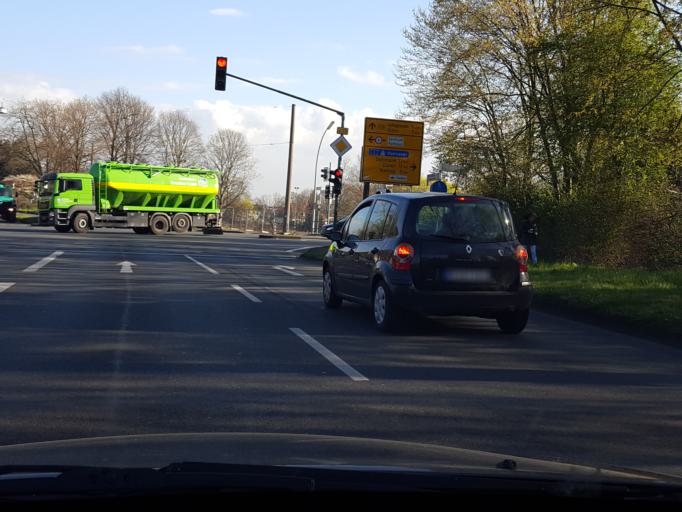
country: DE
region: North Rhine-Westphalia
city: Datteln
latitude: 51.6554
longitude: 7.3522
